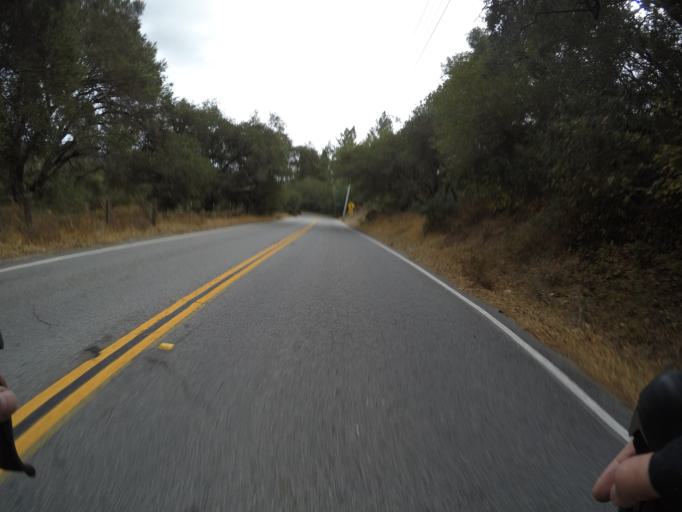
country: US
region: California
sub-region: Santa Cruz County
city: Ben Lomond
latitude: 37.0828
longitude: -122.0642
